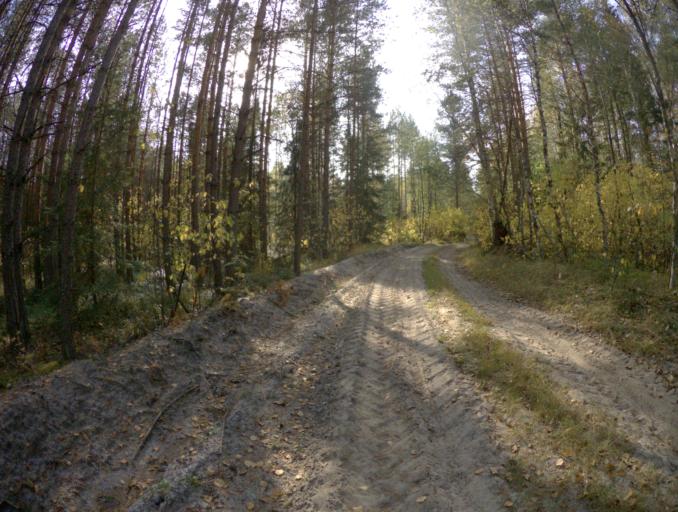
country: RU
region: Vladimir
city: Sobinka
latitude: 55.9285
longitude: 40.0831
